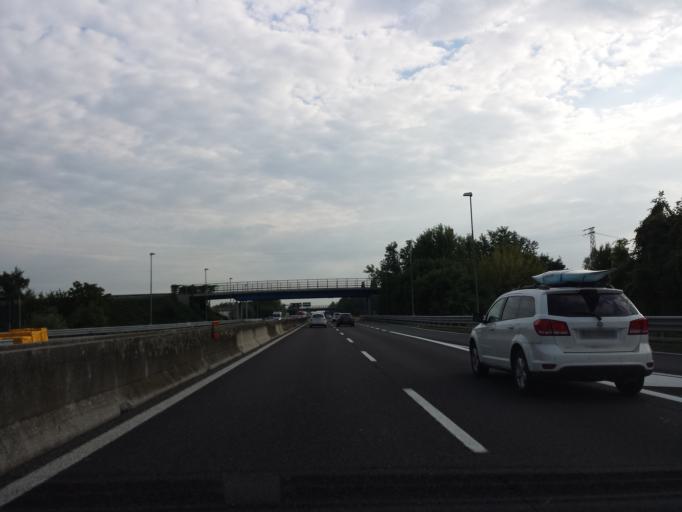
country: IT
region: Veneto
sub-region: Provincia di Padova
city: Pernumia
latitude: 45.2388
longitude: 11.7745
